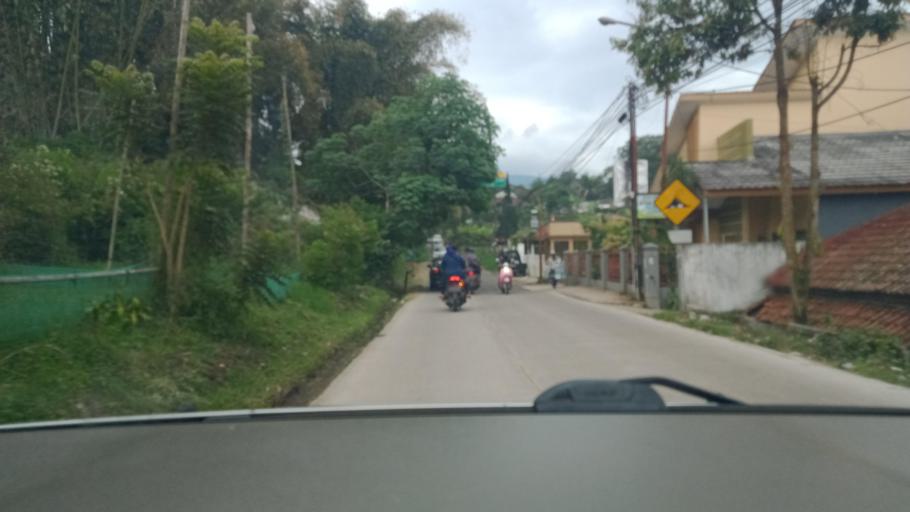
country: ID
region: West Java
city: Lembang
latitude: -6.8259
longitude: 107.5972
